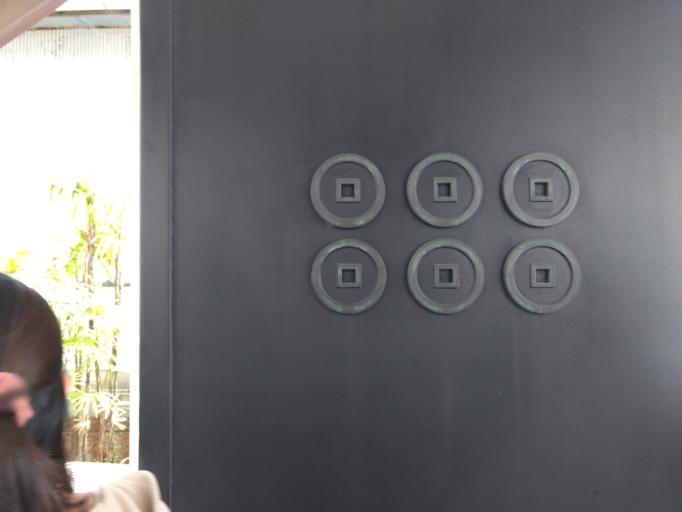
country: JP
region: Osaka
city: Osaka-shi
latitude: 34.6730
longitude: 135.5270
